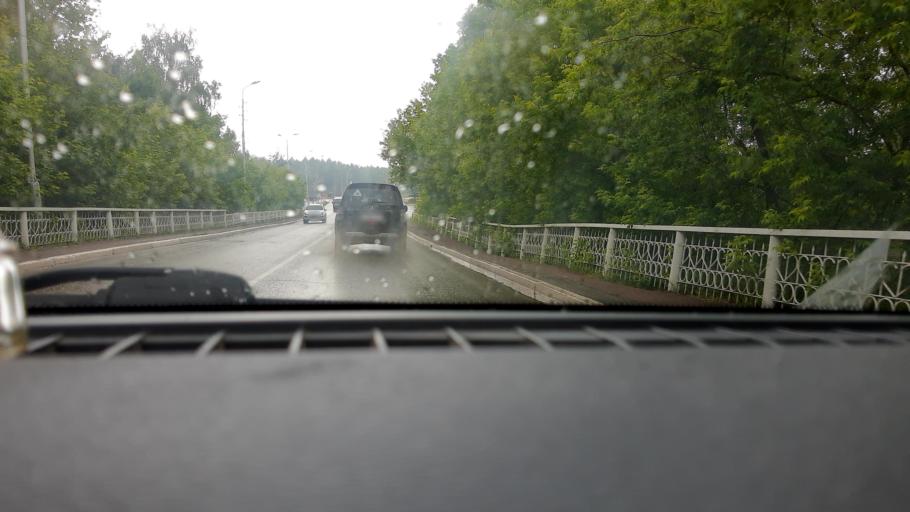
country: RU
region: Bashkortostan
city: Belebey
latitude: 54.1148
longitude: 54.1032
